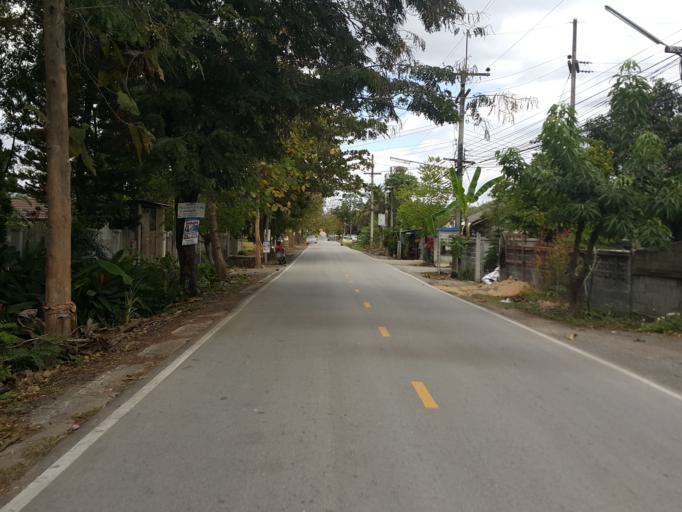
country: TH
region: Chiang Mai
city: San Sai
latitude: 18.8551
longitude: 99.1422
